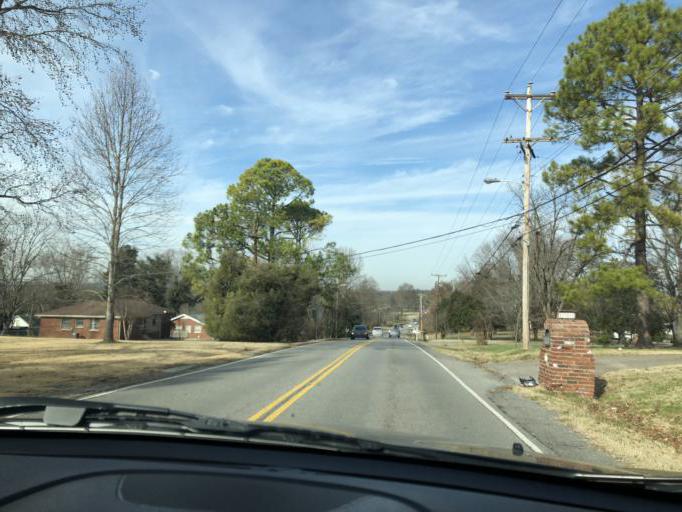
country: US
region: Tennessee
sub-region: Davidson County
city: Lakewood
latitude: 36.1997
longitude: -86.6759
